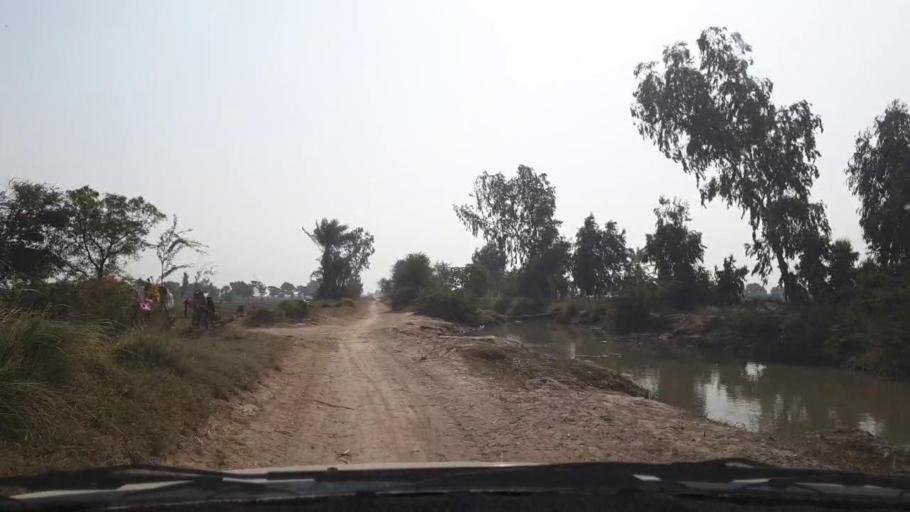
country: PK
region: Sindh
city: Tando Muhammad Khan
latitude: 25.0771
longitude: 68.3622
